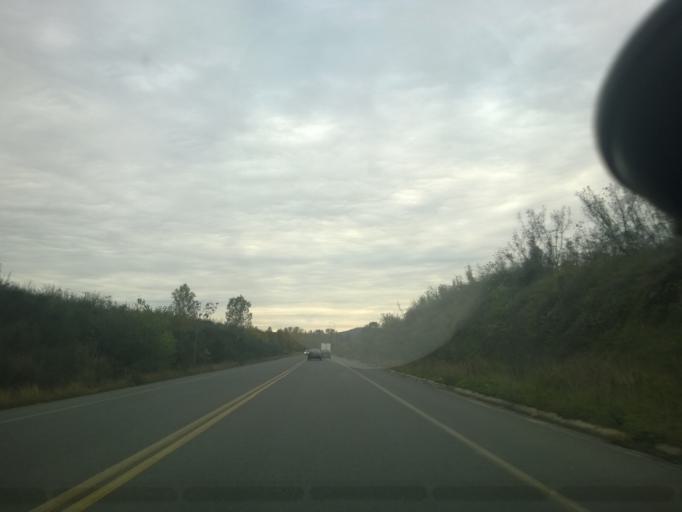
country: GR
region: Central Macedonia
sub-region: Nomos Pellis
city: Aridaia
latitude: 40.9451
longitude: 22.0817
